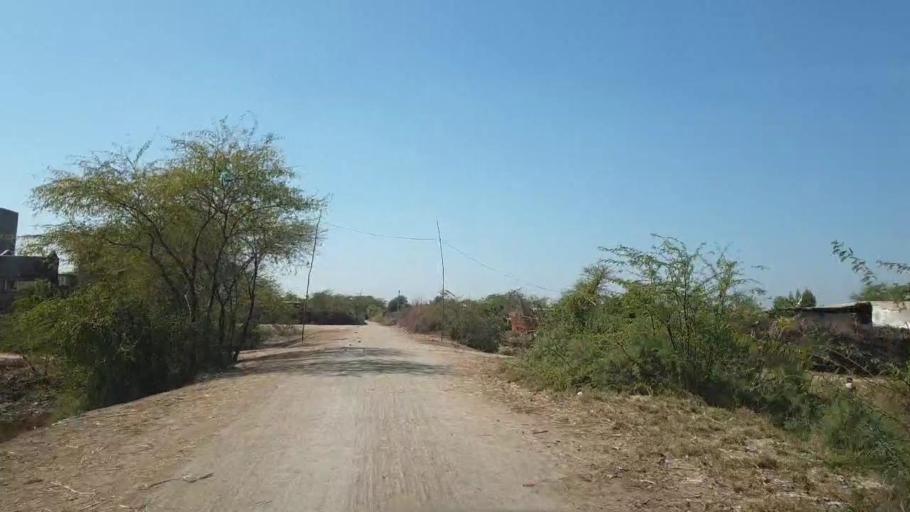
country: PK
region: Sindh
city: Mirpur Khas
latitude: 25.6053
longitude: 69.0803
